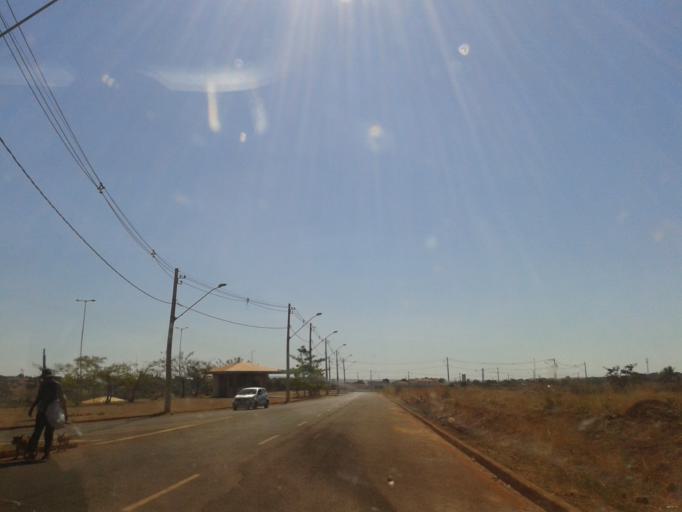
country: BR
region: Minas Gerais
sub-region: Ituiutaba
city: Ituiutaba
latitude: -19.0023
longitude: -49.4754
